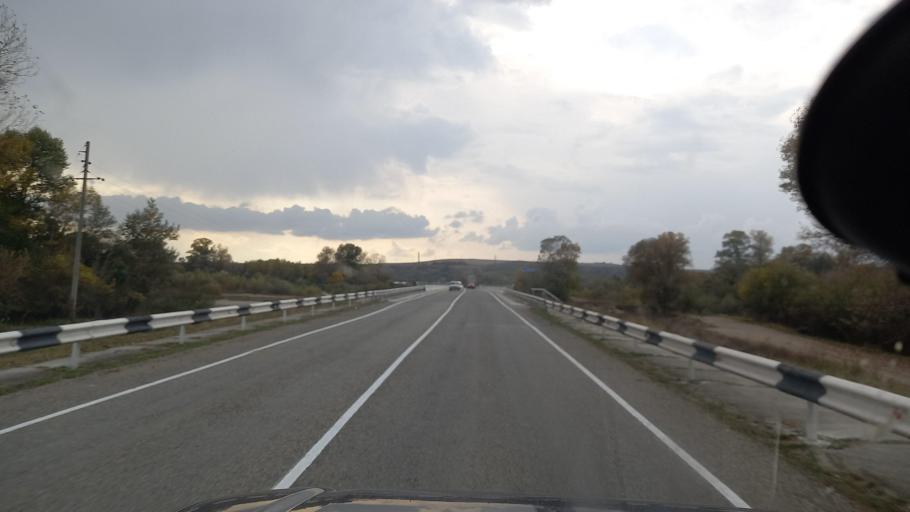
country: RU
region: Krasnodarskiy
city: Mostovskoy
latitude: 44.3911
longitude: 40.7472
